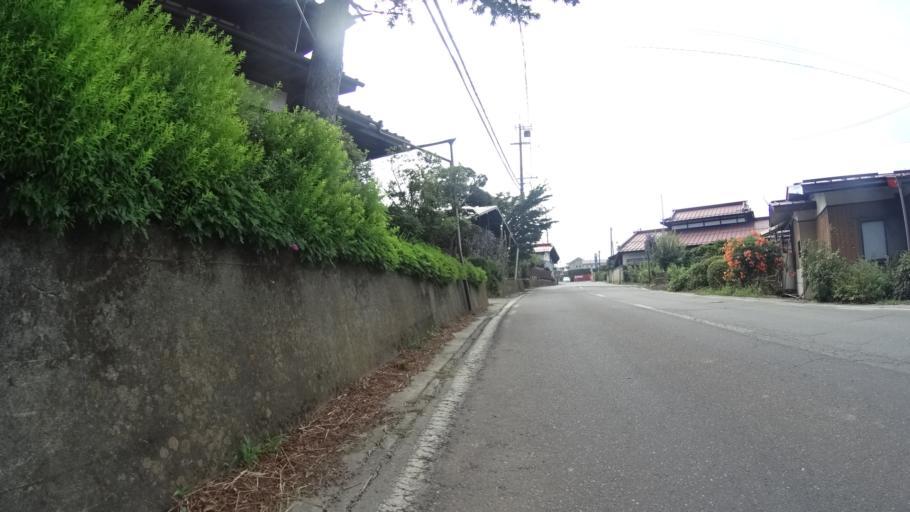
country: JP
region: Nagano
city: Chino
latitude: 35.9552
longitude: 138.2366
